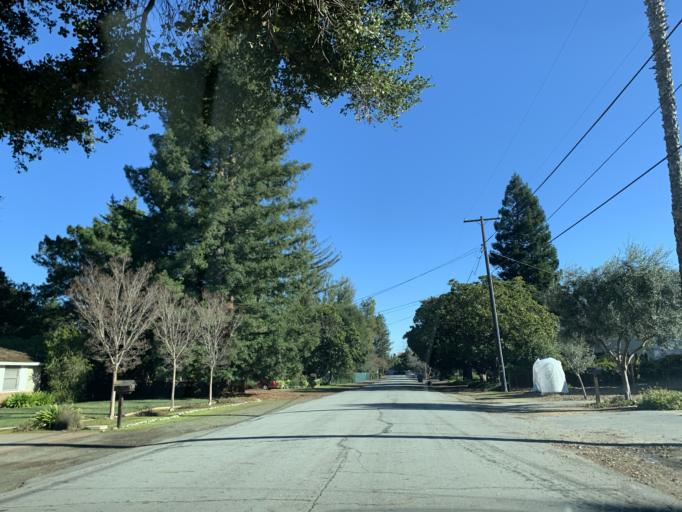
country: US
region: California
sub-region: Santa Clara County
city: Los Altos
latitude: 37.3874
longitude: -122.0991
